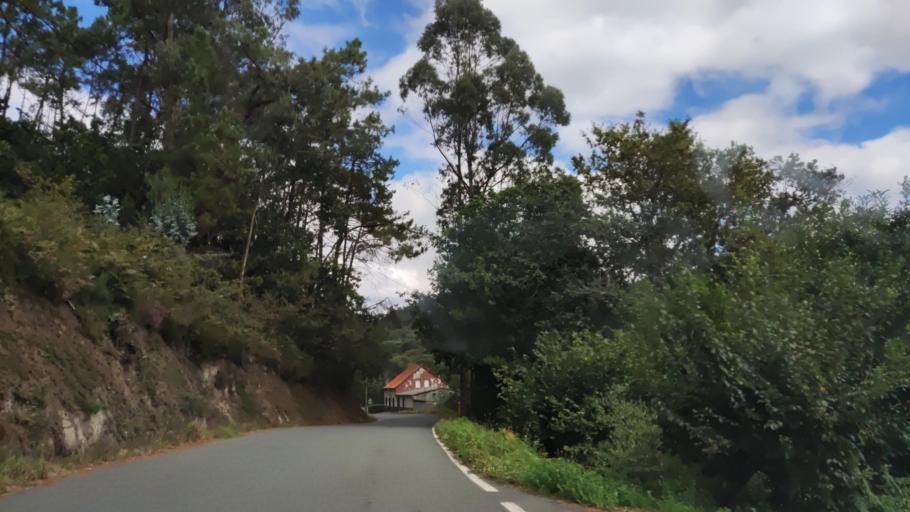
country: ES
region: Galicia
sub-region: Provincia da Coruna
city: Rois
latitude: 42.7399
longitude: -8.7003
